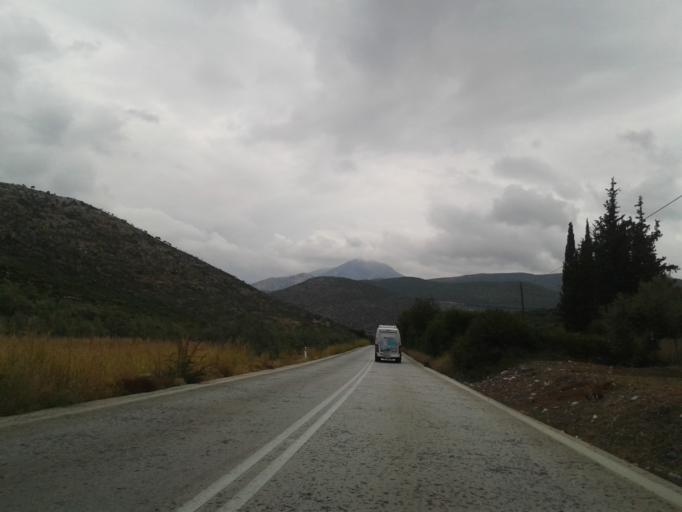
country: GR
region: Peloponnese
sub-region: Nomos Korinthias
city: Ayios Vasilios
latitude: 37.7907
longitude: 22.7381
